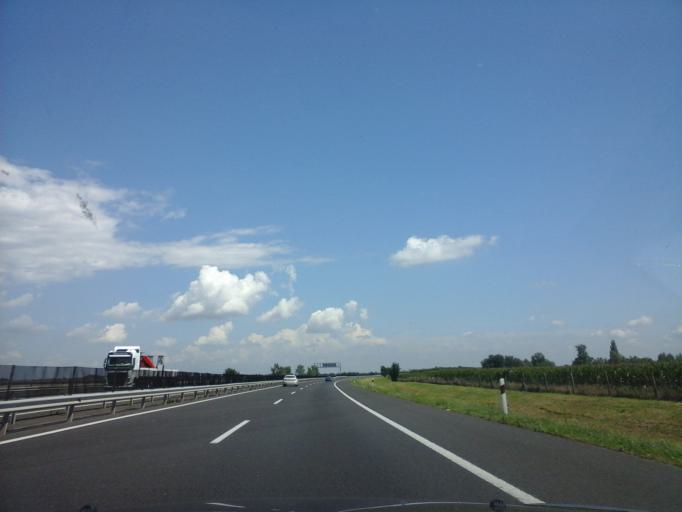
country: HU
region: Borsod-Abauj-Zemplen
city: Mezokeresztes
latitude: 47.8567
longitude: 20.7533
